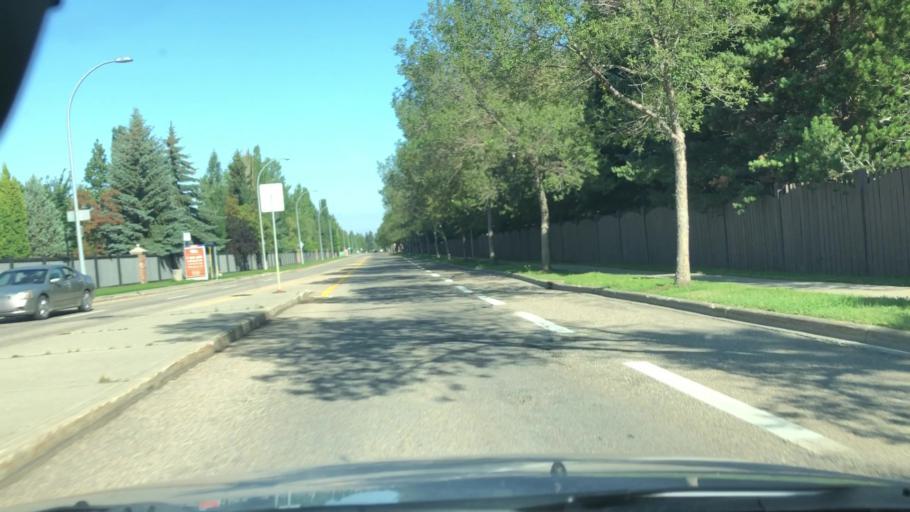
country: CA
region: Alberta
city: Edmonton
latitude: 53.4726
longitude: -113.5950
